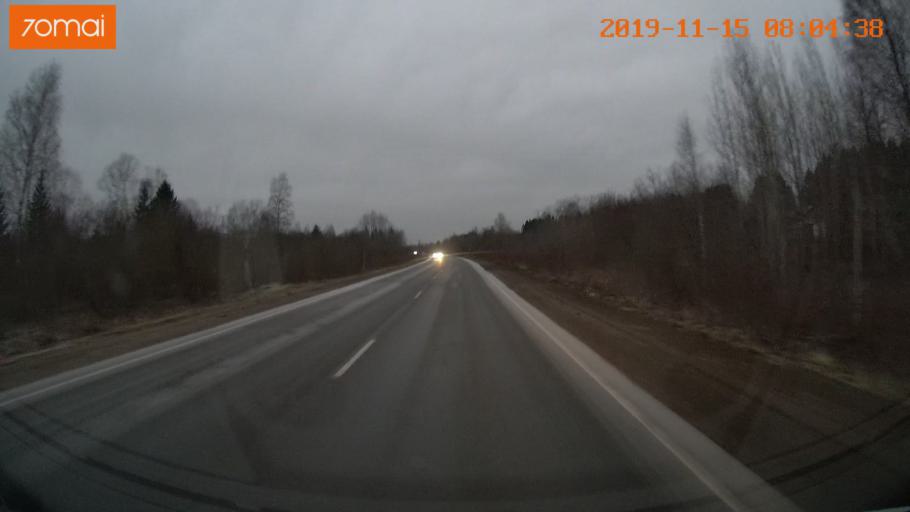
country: RU
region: Vologda
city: Cherepovets
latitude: 59.0101
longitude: 38.0728
